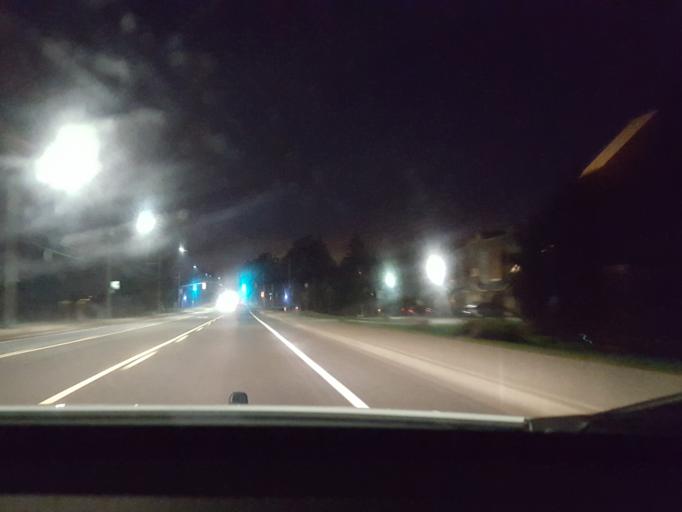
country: CA
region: Ontario
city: Hamilton
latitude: 43.2118
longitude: -79.8916
